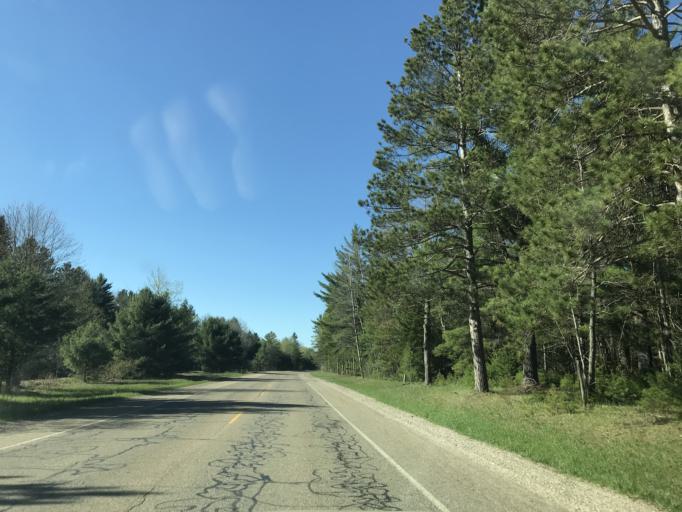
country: US
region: Michigan
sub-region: Crawford County
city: Grayling
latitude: 44.7626
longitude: -84.7541
